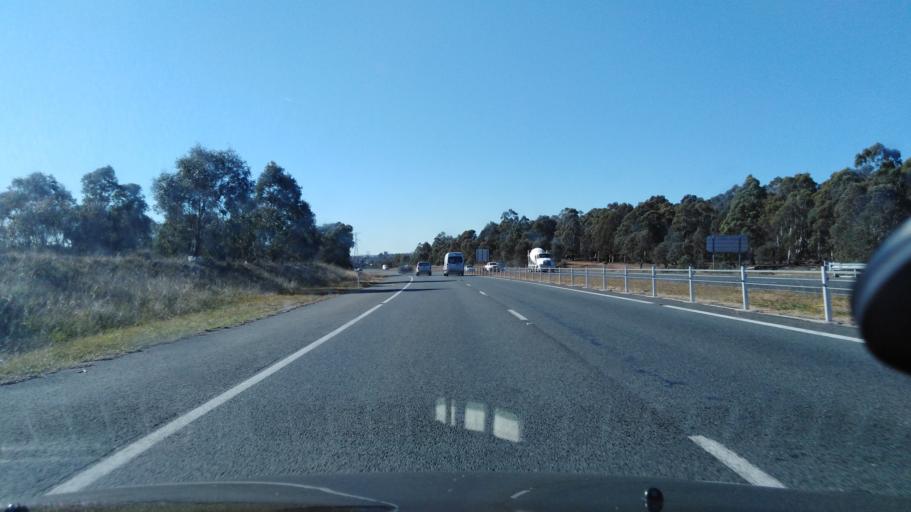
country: AU
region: Australian Capital Territory
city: Kaleen
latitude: -35.2370
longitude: 149.1148
